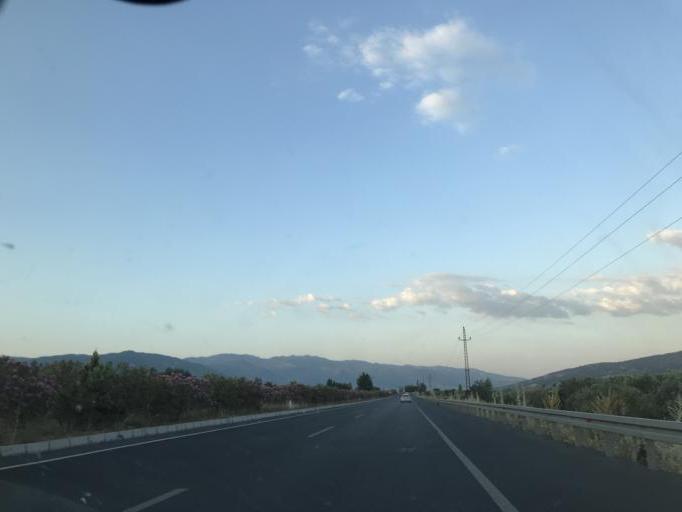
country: TR
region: Aydin
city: Horsunlu
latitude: 37.9256
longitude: 28.6501
